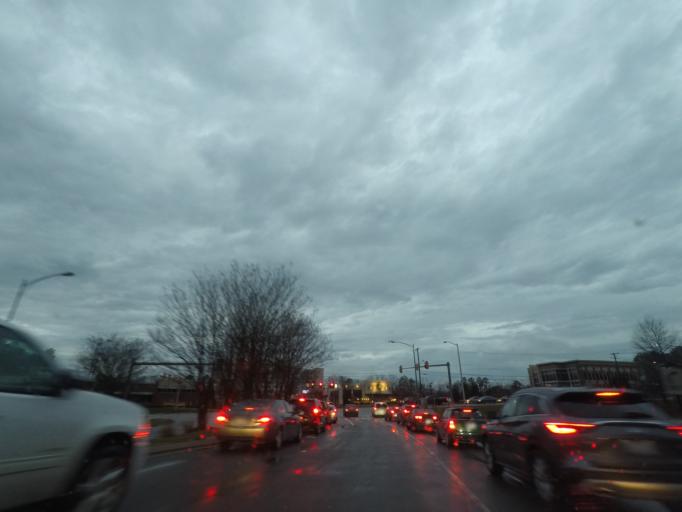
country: US
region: North Carolina
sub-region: Orange County
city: Chapel Hill
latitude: 35.9011
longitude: -78.9588
